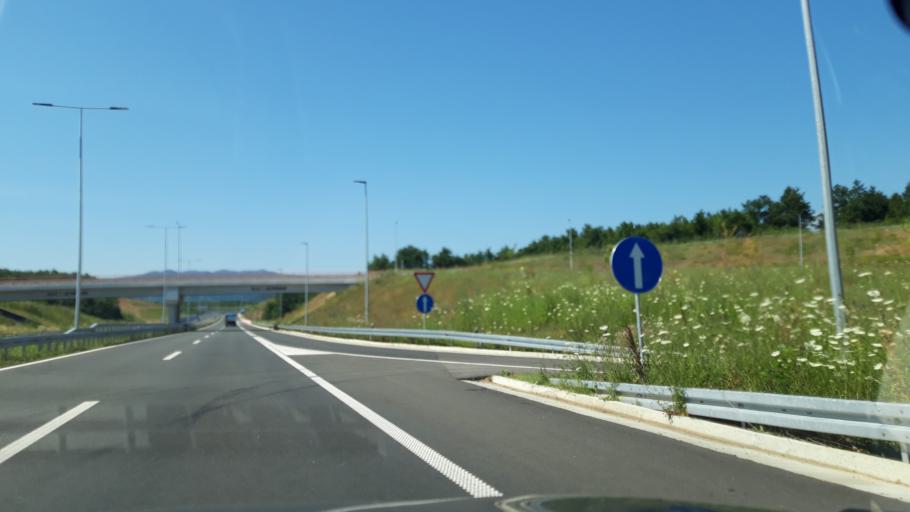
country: RS
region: Central Serbia
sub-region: Pcinjski Okrug
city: Vladicin Han
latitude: 42.7030
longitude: 22.0748
